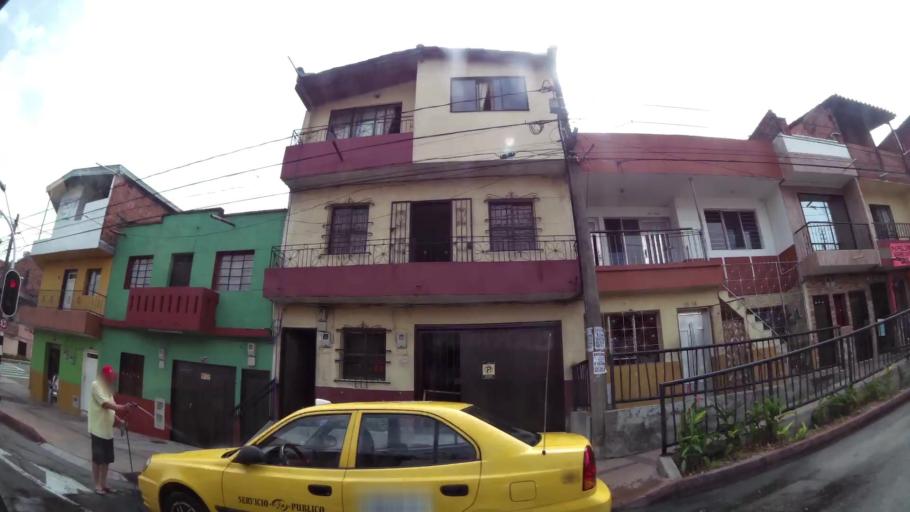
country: CO
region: Antioquia
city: Medellin
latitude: 6.2756
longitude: -75.5527
